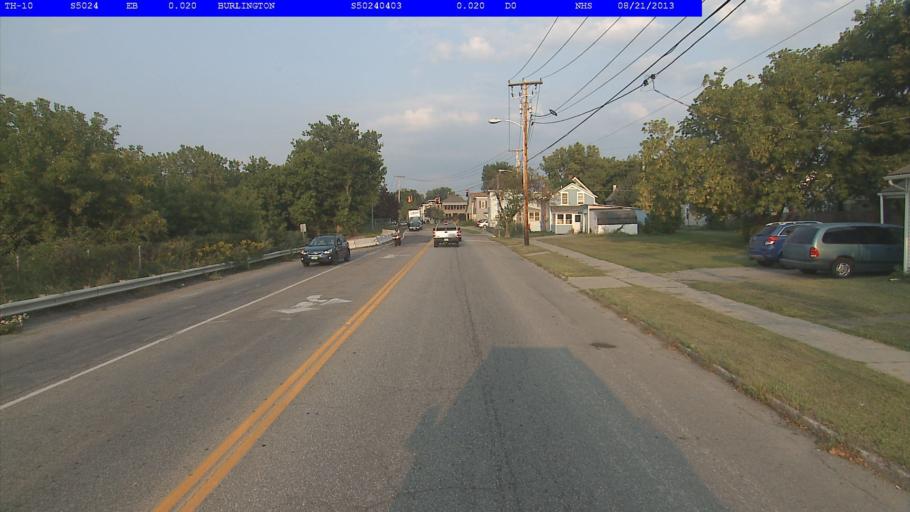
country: US
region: Vermont
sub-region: Chittenden County
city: Burlington
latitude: 44.4875
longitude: -73.2190
